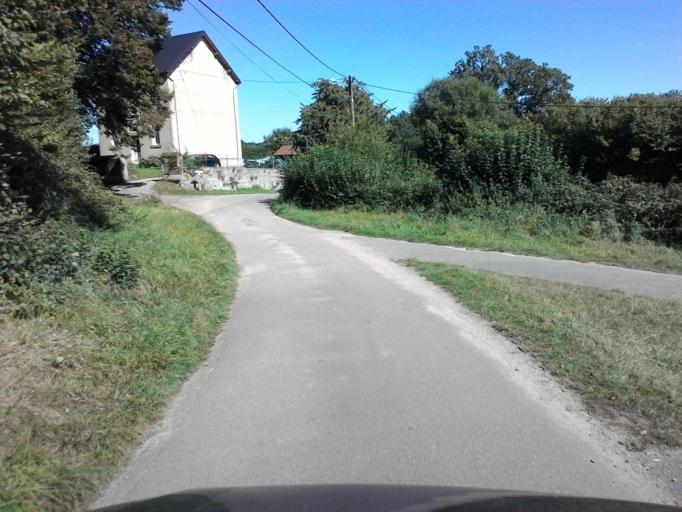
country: FR
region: Bourgogne
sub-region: Departement de la Cote-d'Or
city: Saulieu
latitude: 47.2469
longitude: 4.2001
